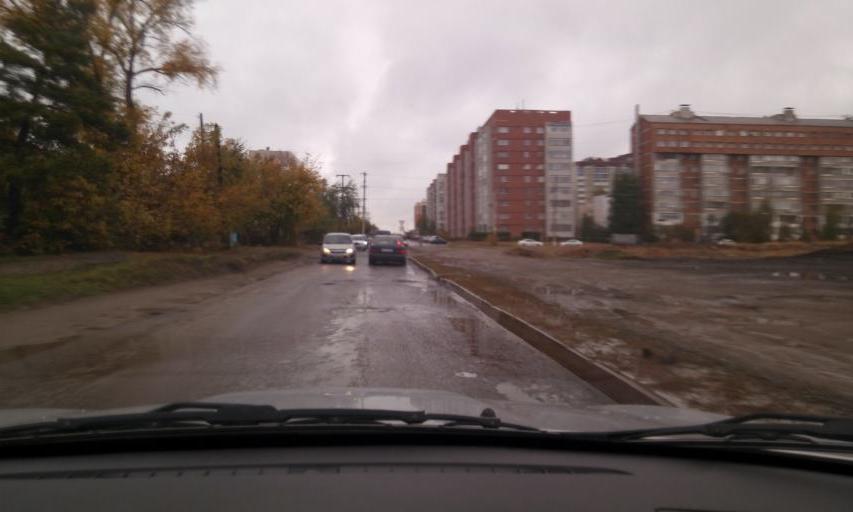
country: KZ
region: Astana Qalasy
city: Astana
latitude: 51.1638
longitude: 71.4004
